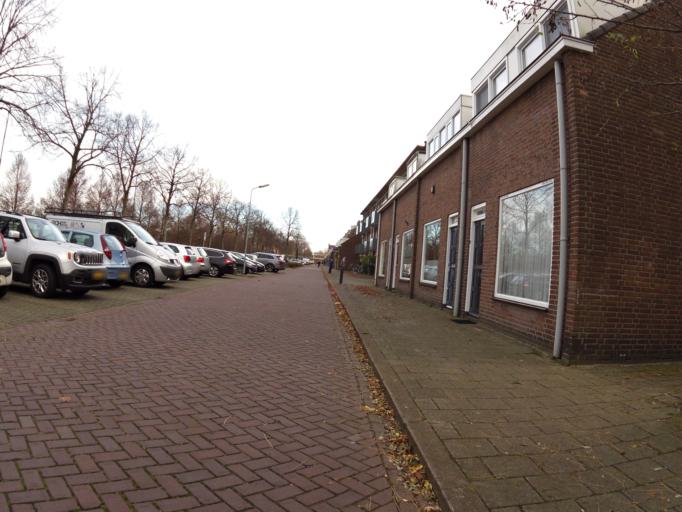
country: NL
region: North Brabant
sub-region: Gemeente 's-Hertogenbosch
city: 's-Hertogenbosch
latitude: 51.6874
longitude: 5.3188
